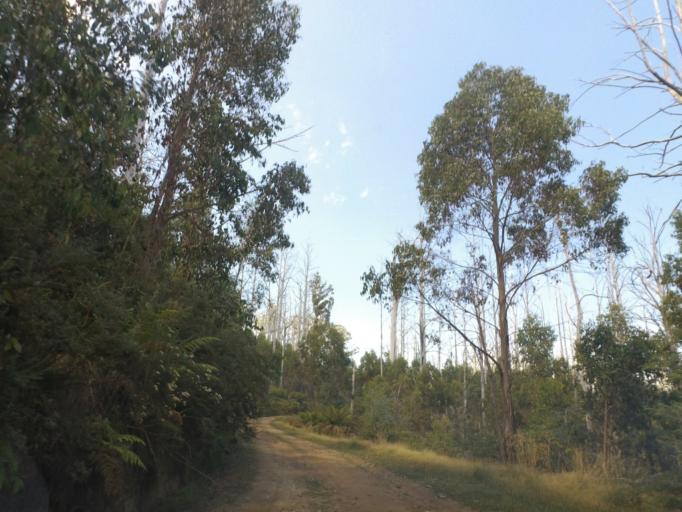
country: AU
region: Victoria
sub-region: Murrindindi
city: Alexandra
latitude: -37.4789
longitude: 145.8363
